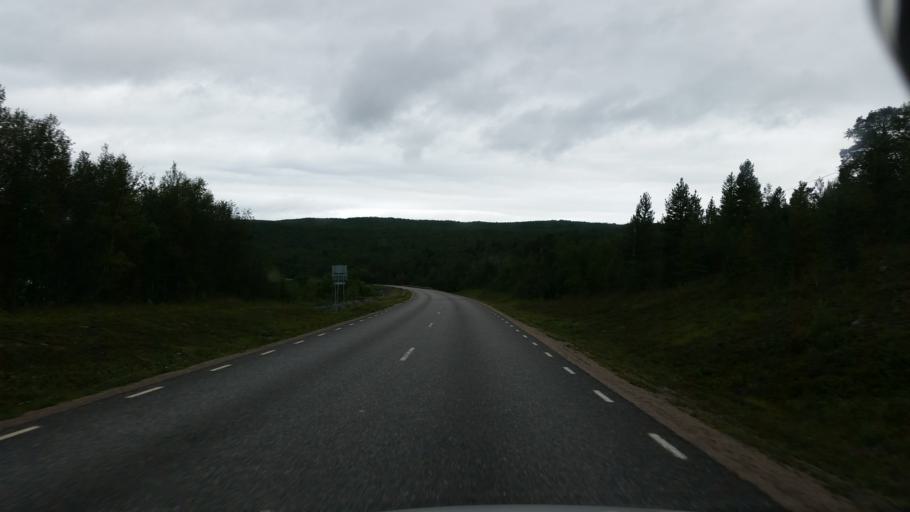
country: SE
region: Norrbotten
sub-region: Arjeplogs Kommun
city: Arjeplog
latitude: 66.4490
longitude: 16.7768
